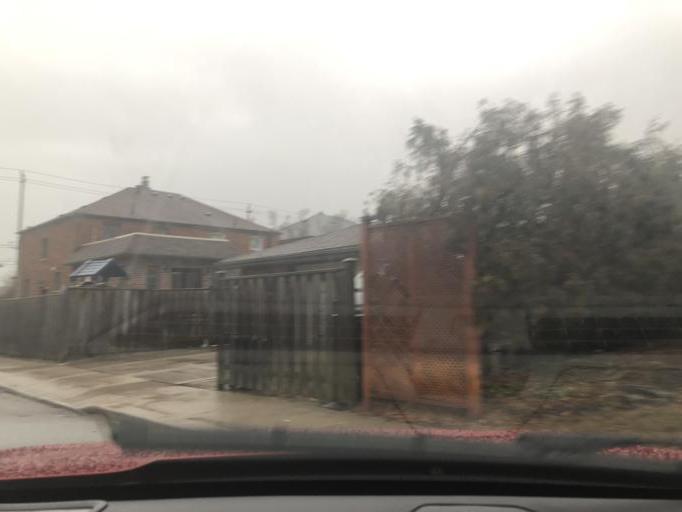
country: CA
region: Ontario
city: Toronto
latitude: 43.6929
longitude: -79.3359
